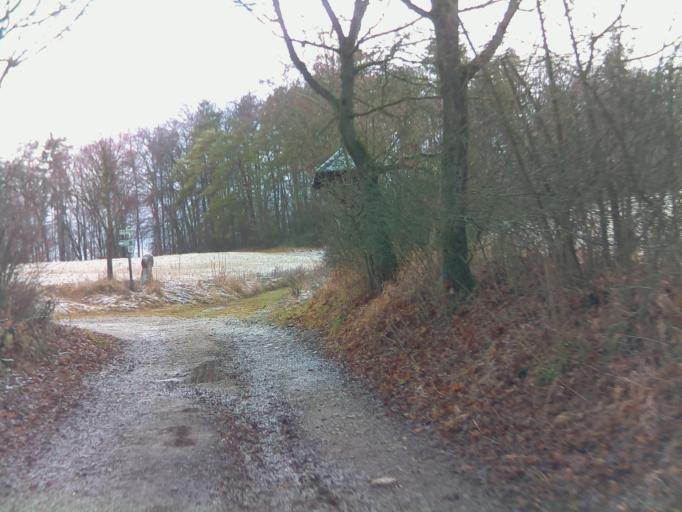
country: DE
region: Thuringia
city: Reinstadt
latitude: 50.7869
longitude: 11.4641
